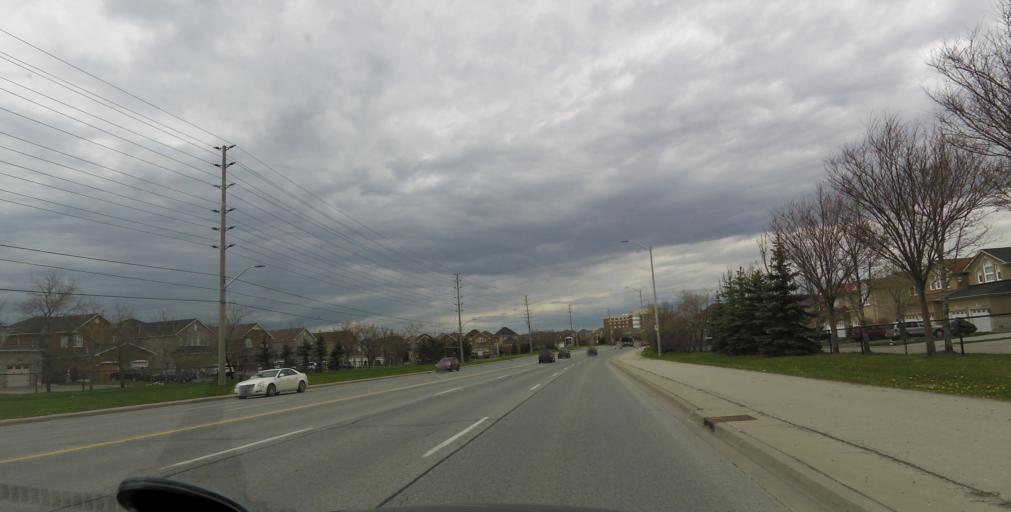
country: CA
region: Ontario
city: Mississauga
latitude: 43.6013
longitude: -79.6838
